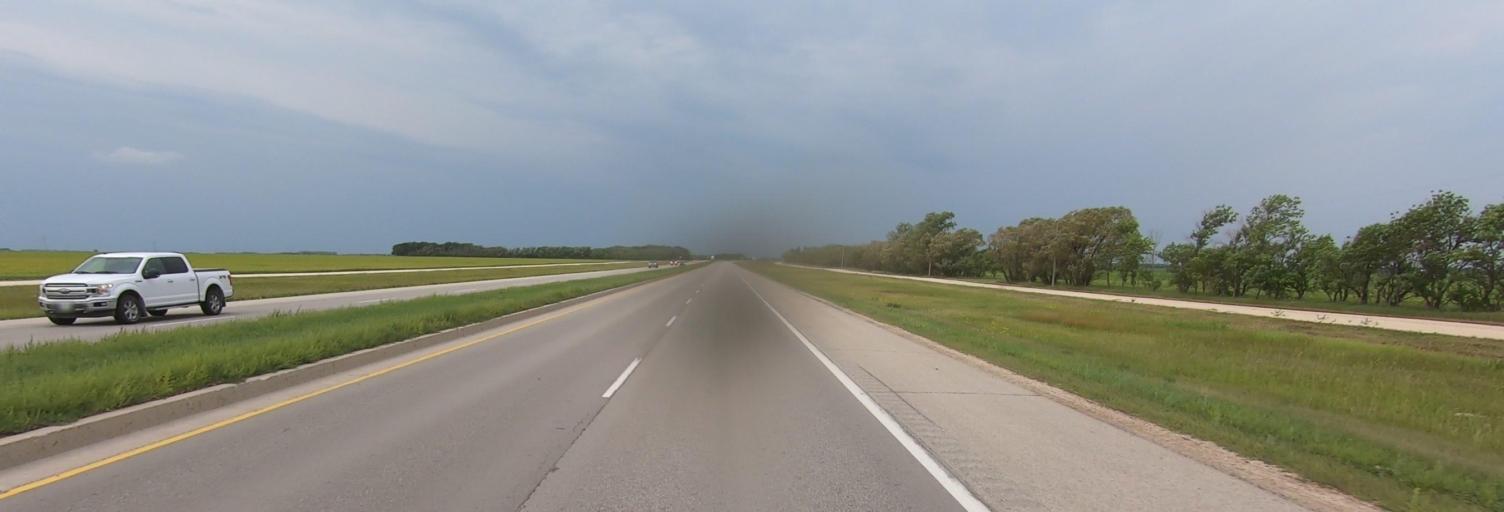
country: CA
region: Manitoba
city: Headingley
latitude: 49.7680
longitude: -97.2783
